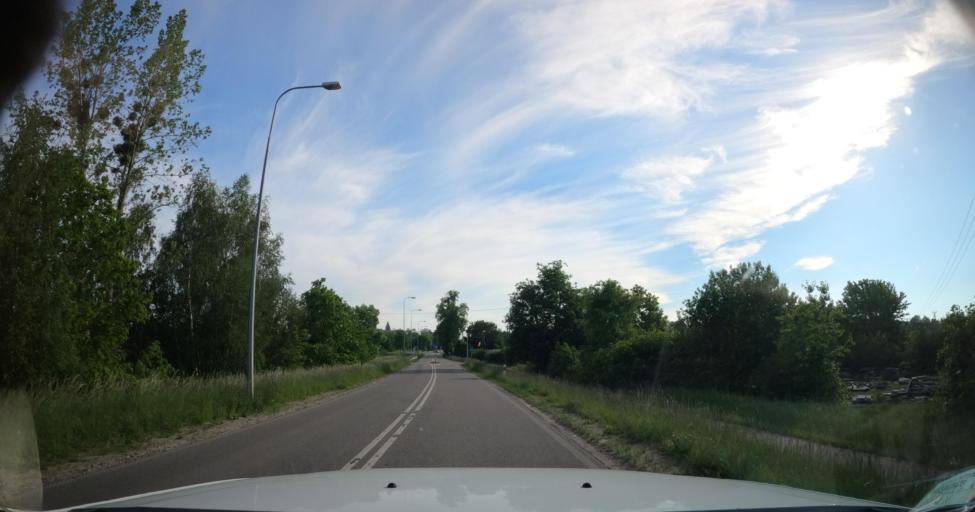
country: PL
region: Warmian-Masurian Voivodeship
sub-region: Powiat elblaski
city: Paslek
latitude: 54.0743
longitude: 19.6641
